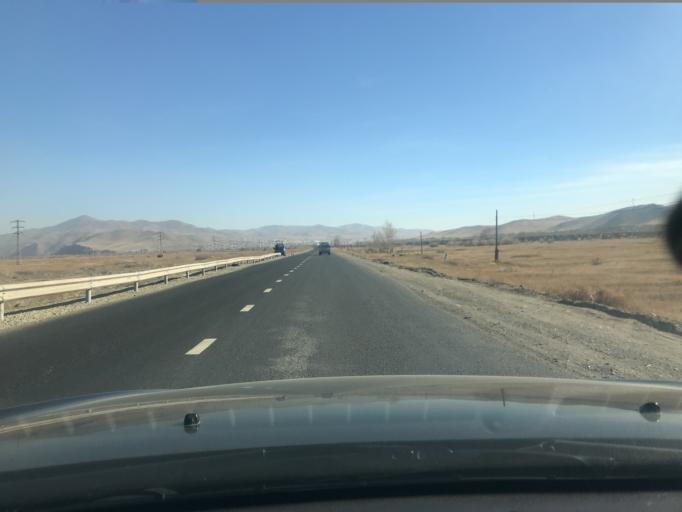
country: MN
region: Ulaanbaatar
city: Ulaanbaatar
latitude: 47.8993
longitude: 107.0391
